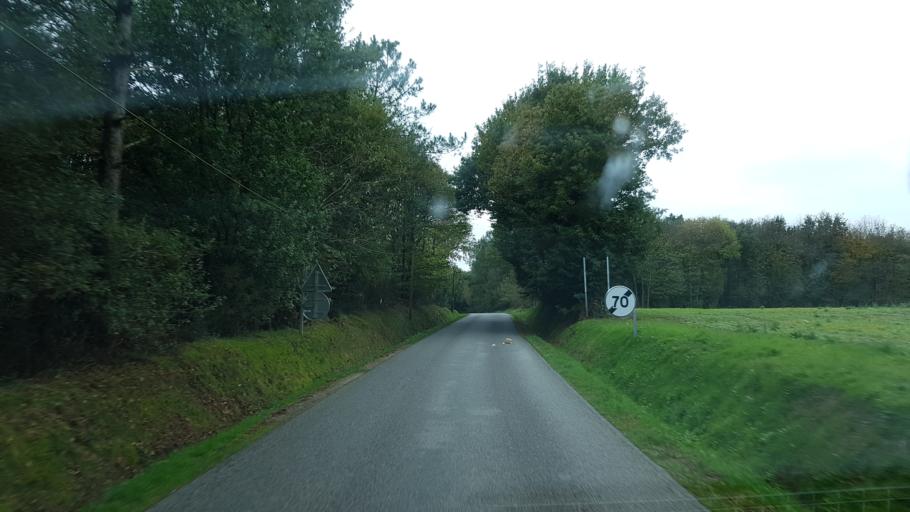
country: FR
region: Brittany
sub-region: Departement du Morbihan
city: Molac
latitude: 47.7802
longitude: -2.4629
